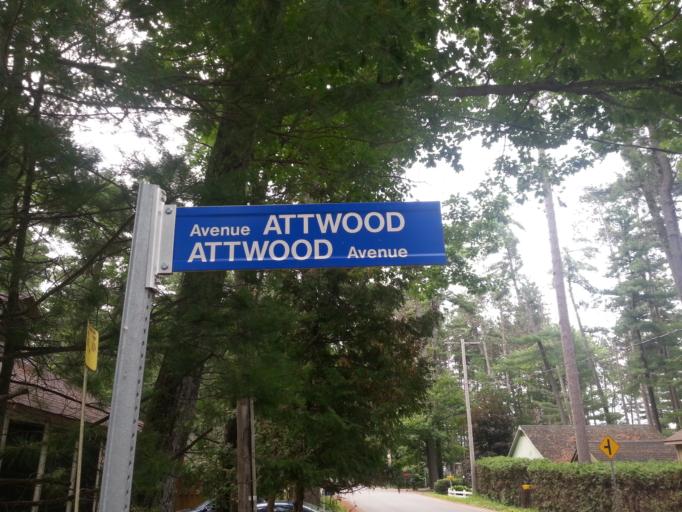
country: CA
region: Quebec
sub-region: Outaouais
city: Shawville
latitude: 45.5171
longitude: -76.4170
